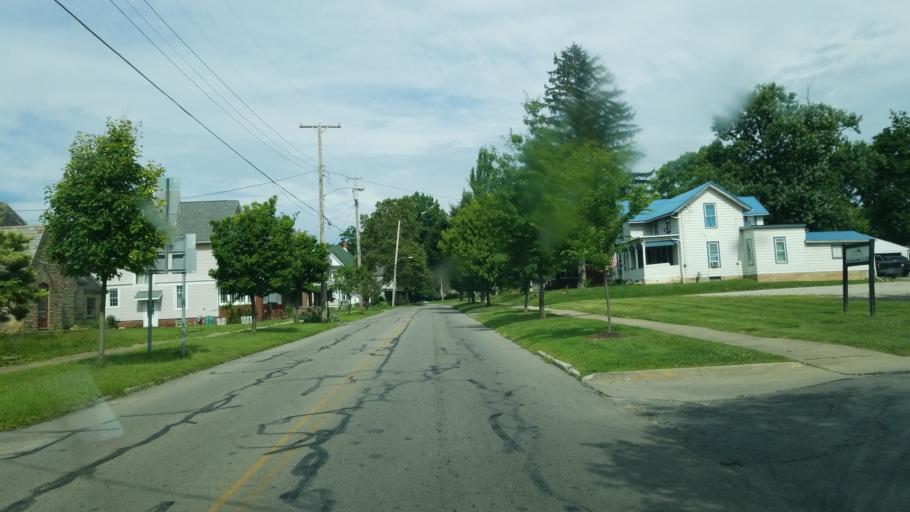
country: US
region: Ohio
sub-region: Ashland County
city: Ashland
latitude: 40.8698
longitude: -82.3193
